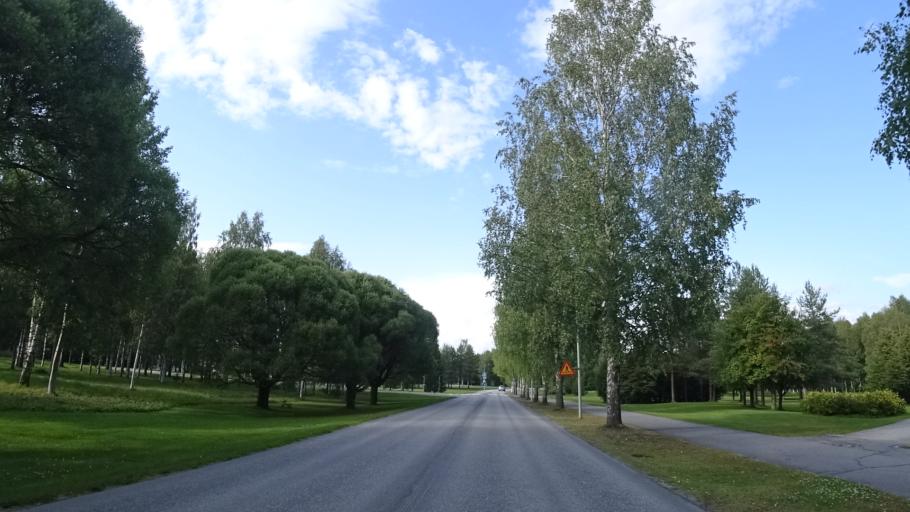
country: FI
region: North Karelia
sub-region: Pielisen Karjala
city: Lieksa
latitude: 63.3260
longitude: 30.0225
